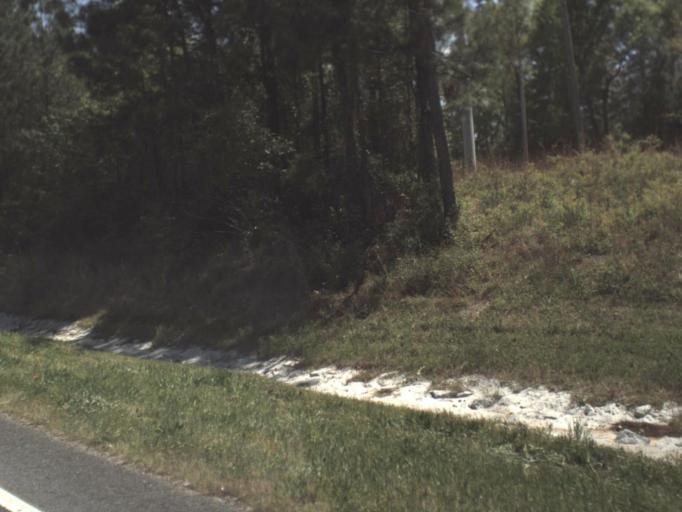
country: US
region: Florida
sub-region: Escambia County
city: Century
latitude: 30.9556
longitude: -87.2075
